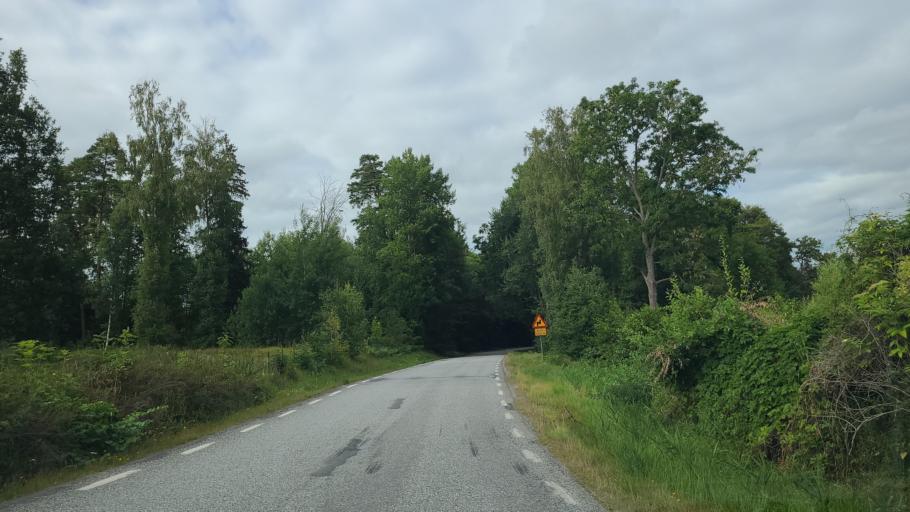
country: SE
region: Stockholm
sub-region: Upplands-Bro Kommun
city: Bro
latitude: 59.4904
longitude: 17.5670
